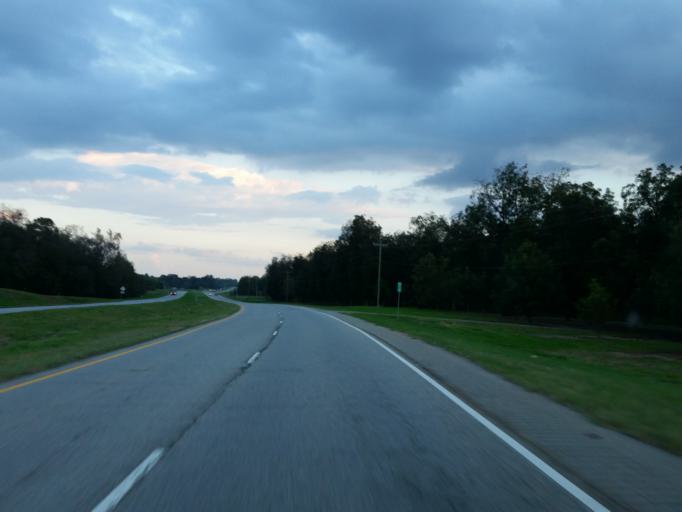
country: US
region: Georgia
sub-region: Pulaski County
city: Hawkinsville
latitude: 32.3145
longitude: -83.5325
